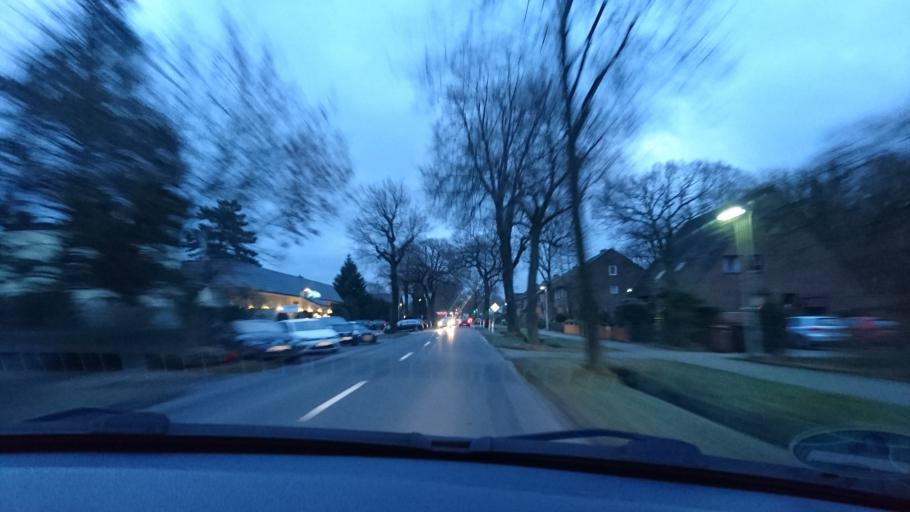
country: DE
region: Schleswig-Holstein
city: Ellerbek
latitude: 53.6239
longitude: 9.8801
